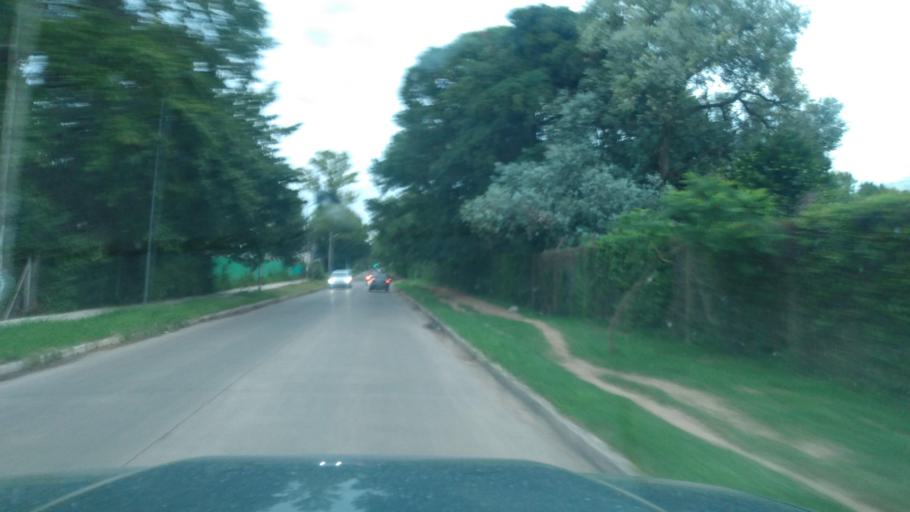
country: AR
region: Buenos Aires
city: Hurlingham
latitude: -34.5601
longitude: -58.7240
